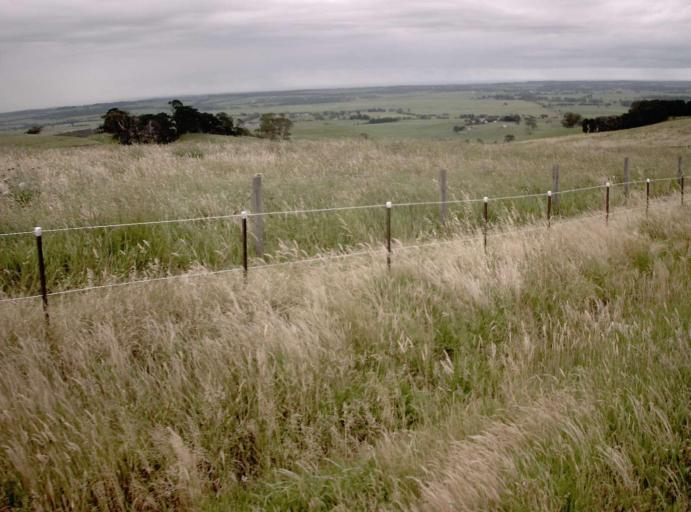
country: AU
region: Victoria
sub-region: Bass Coast
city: North Wonthaggi
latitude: -38.4991
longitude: 145.7283
